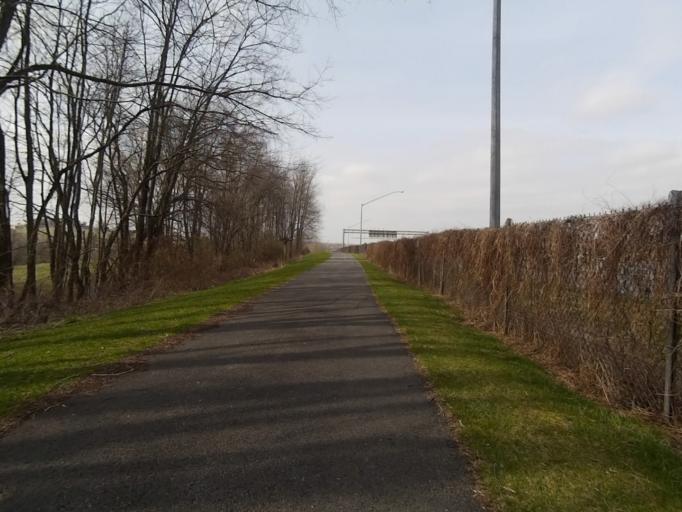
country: US
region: Pennsylvania
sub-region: Centre County
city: Houserville
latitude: 40.8141
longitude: -77.8315
